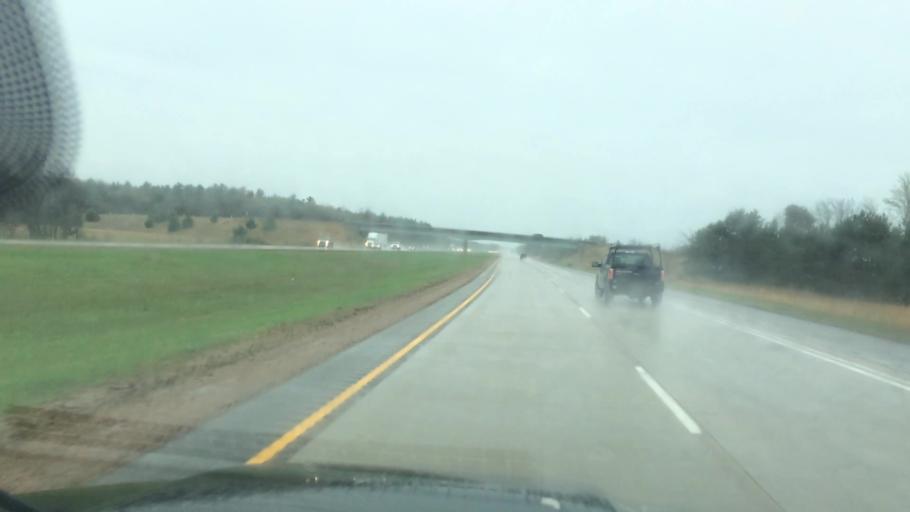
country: US
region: Wisconsin
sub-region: Portage County
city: Stevens Point
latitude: 44.6301
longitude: -89.6343
